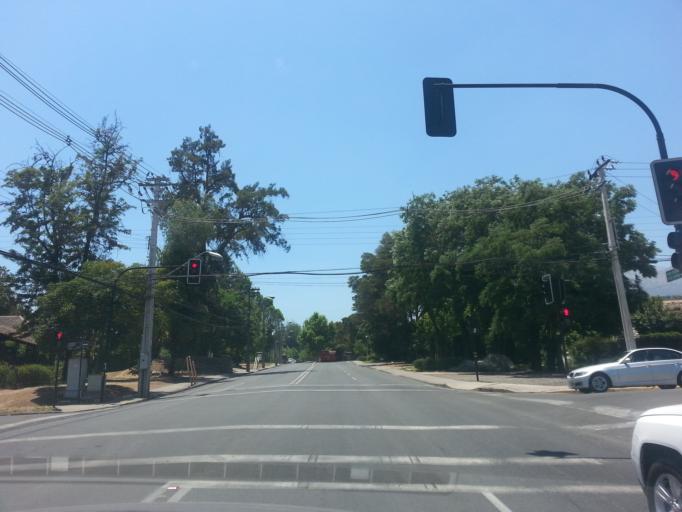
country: CL
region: Santiago Metropolitan
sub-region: Provincia de Santiago
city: Villa Presidente Frei, Nunoa, Santiago, Chile
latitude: -33.4056
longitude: -70.5403
